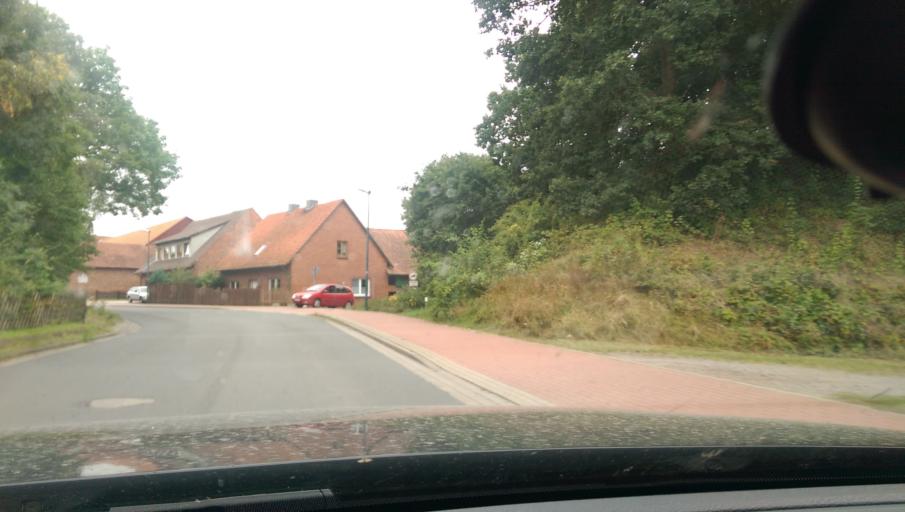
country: DE
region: Lower Saxony
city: Rehburg-Loccum
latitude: 52.4567
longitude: 9.1572
